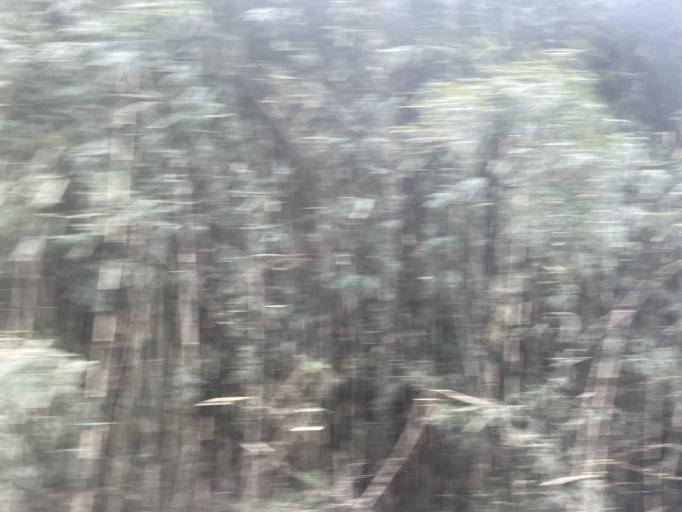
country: JP
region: Chiba
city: Yachimata
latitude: 35.6314
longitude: 140.3576
